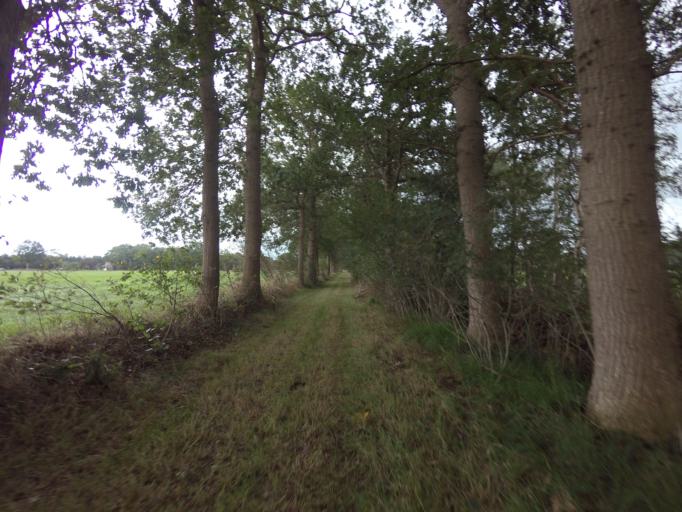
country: NL
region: Friesland
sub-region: Gemeente Weststellingwerf
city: Noordwolde
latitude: 52.9530
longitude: 6.1718
